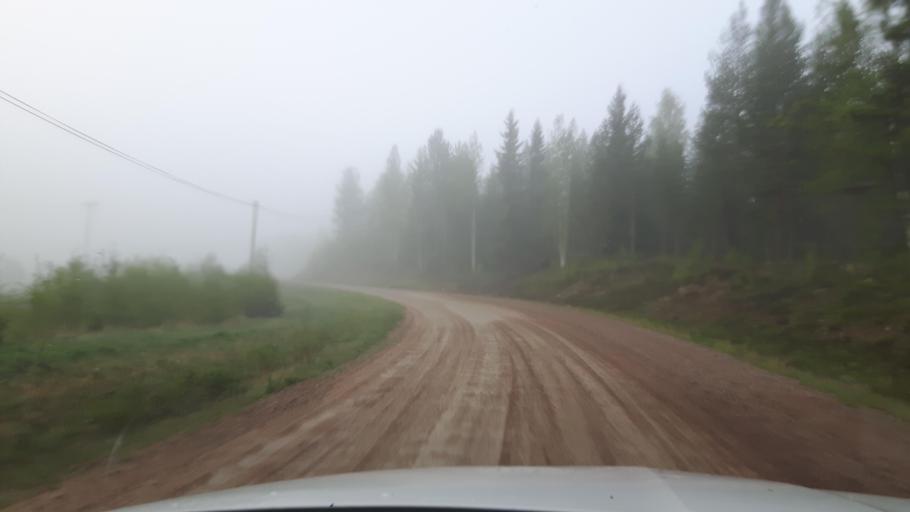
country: SE
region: Vaesternorrland
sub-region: Ange Kommun
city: Ange
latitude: 62.1783
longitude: 15.6324
